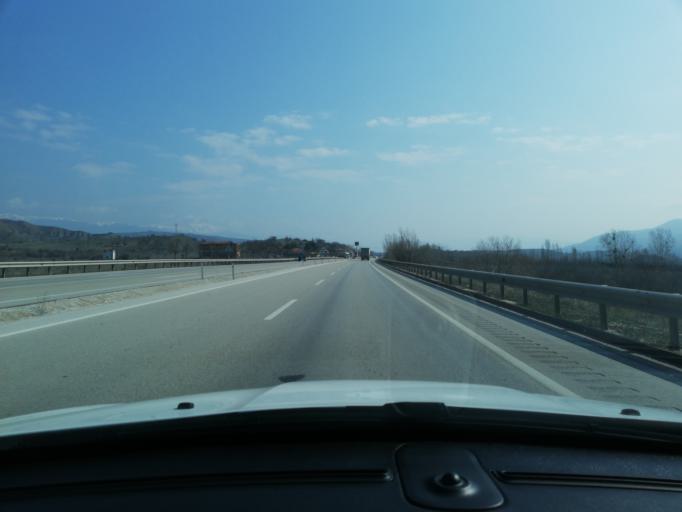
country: TR
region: Cankiri
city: Beloren
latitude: 40.8671
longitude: 33.4874
